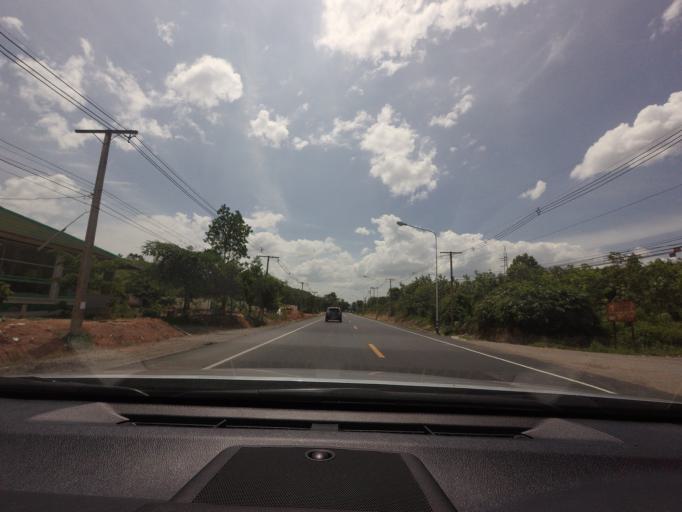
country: TH
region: Yala
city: Krong Pi Nang
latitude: 6.4663
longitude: 101.3279
